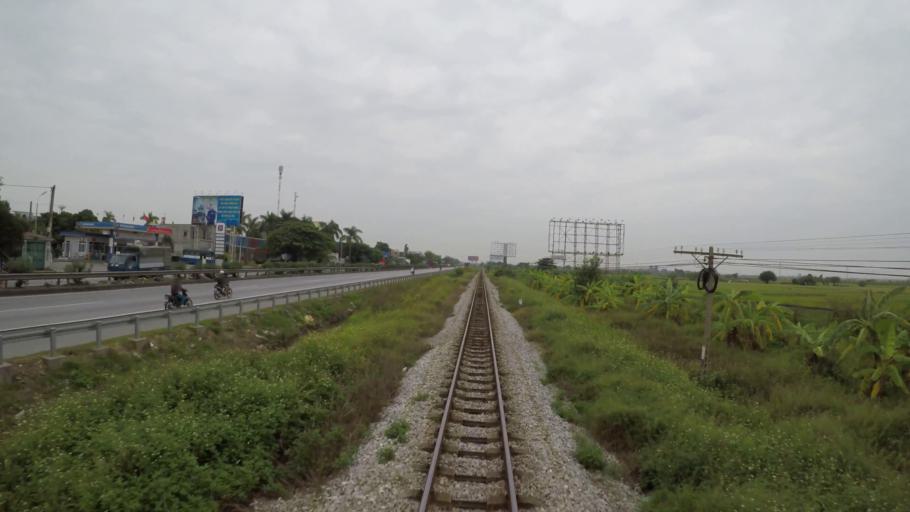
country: VN
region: Hai Duong
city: Phu Thai
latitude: 20.9382
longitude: 106.5479
